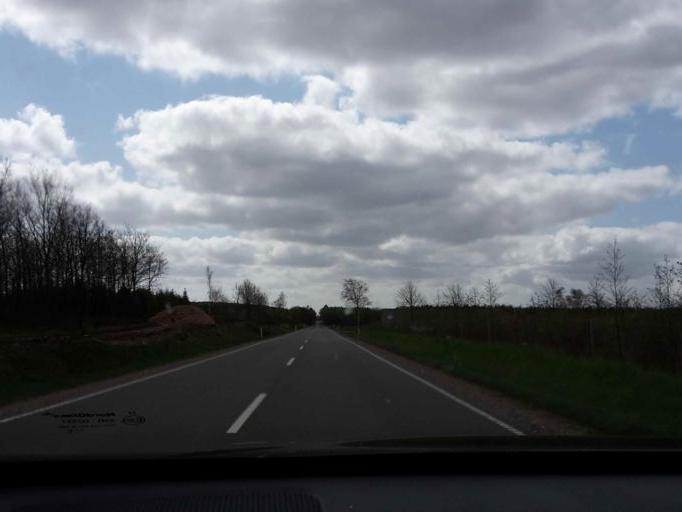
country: DK
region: South Denmark
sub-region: Varde Kommune
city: Olgod
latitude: 55.7052
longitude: 8.6076
